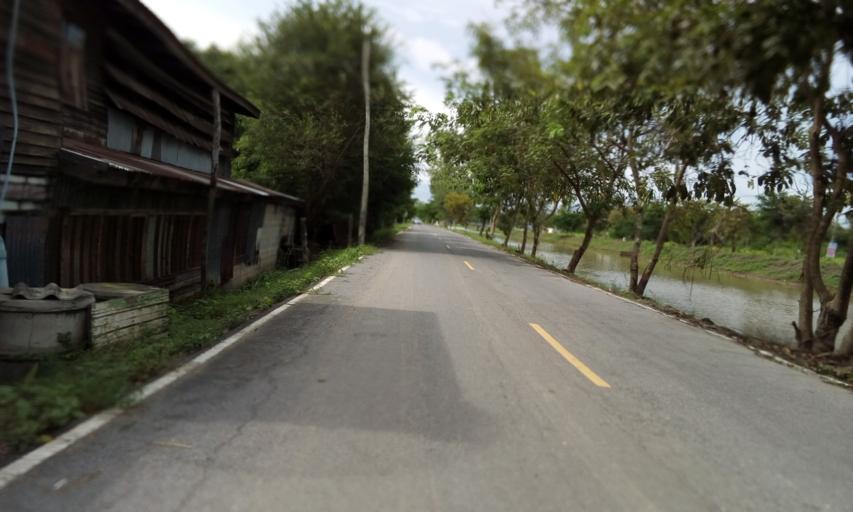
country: TH
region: Pathum Thani
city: Nong Suea
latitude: 14.1057
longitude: 100.8236
